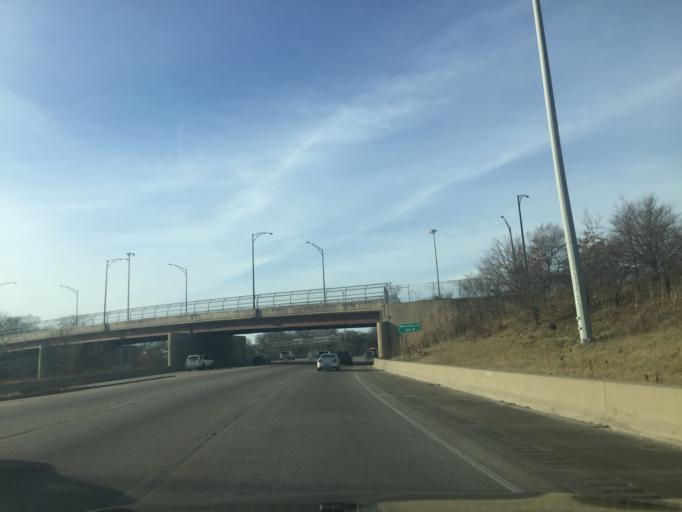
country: US
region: Illinois
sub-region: Cook County
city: Calumet Park
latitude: 41.7160
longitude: -87.6278
